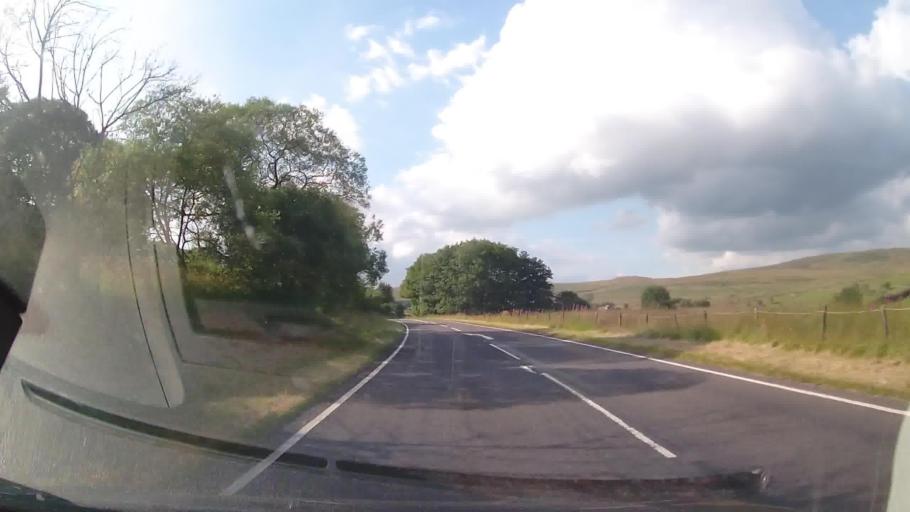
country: GB
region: Wales
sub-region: Gwynedd
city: Bala
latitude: 52.9585
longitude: -3.7214
